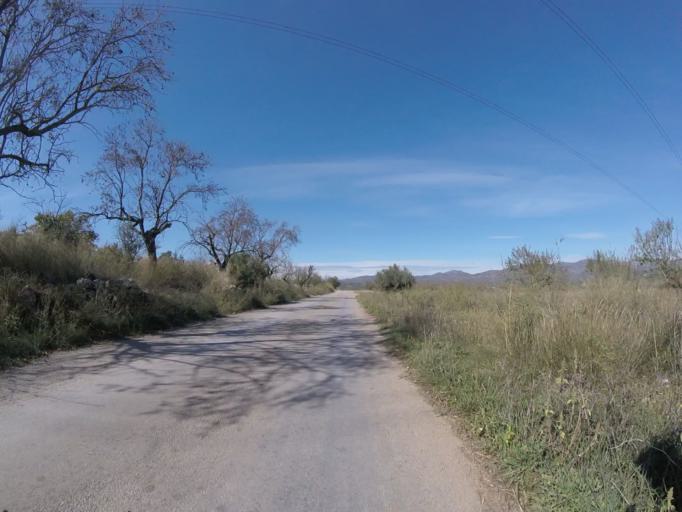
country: ES
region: Valencia
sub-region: Provincia de Castello
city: Benlloch
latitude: 40.2104
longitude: 0.0390
